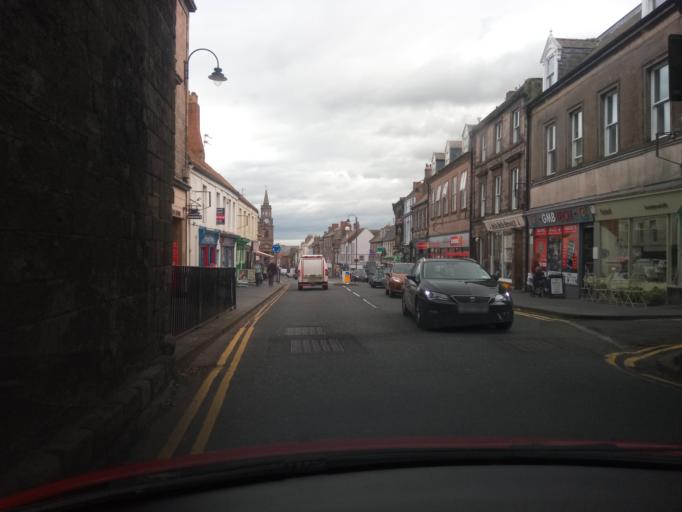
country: GB
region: England
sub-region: Northumberland
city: Berwick-Upon-Tweed
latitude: 55.7710
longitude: -2.0065
